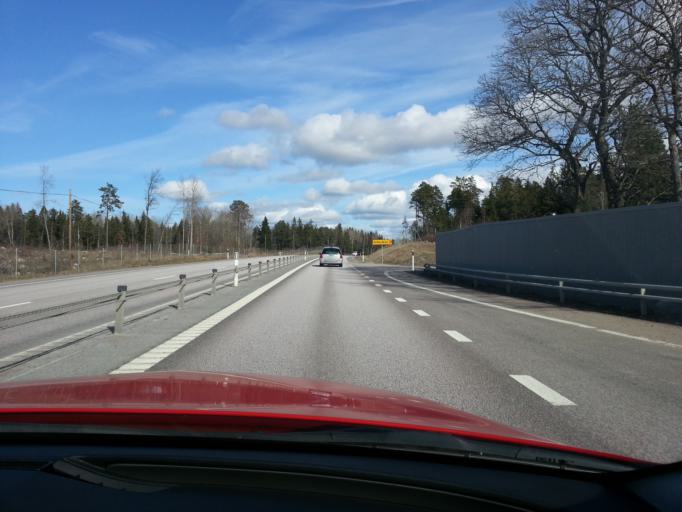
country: SE
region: Uppsala
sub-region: Uppsala Kommun
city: Storvreta
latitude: 59.9195
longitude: 17.7592
